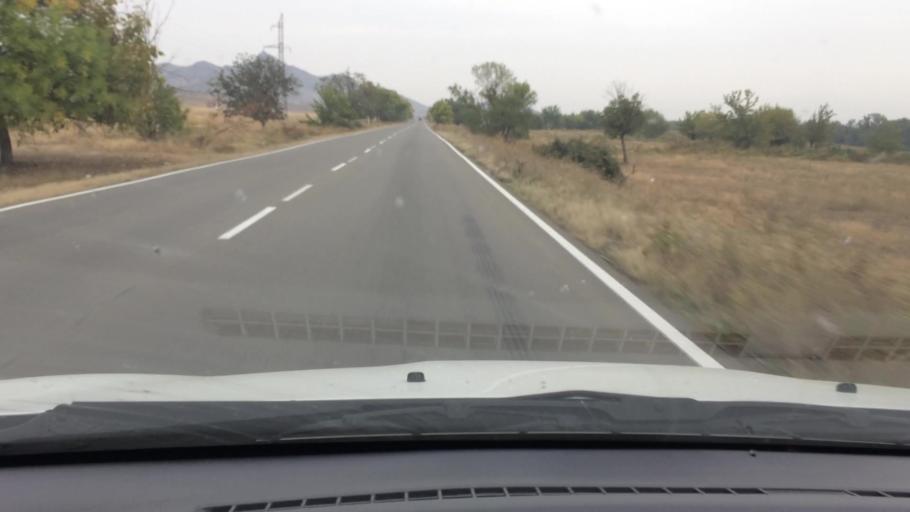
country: GE
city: Naghvarevi
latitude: 41.3323
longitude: 44.8056
